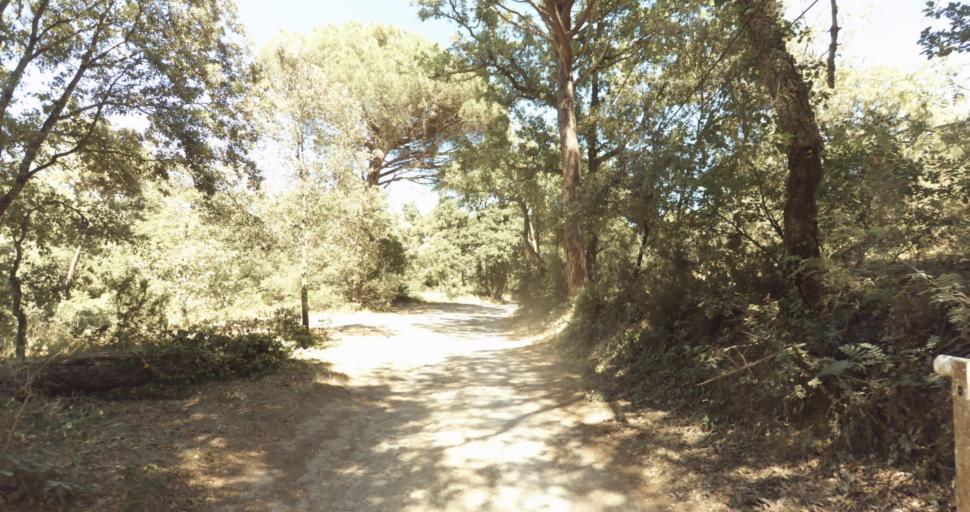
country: FR
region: Provence-Alpes-Cote d'Azur
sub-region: Departement du Var
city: La Croix-Valmer
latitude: 43.2305
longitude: 6.5604
